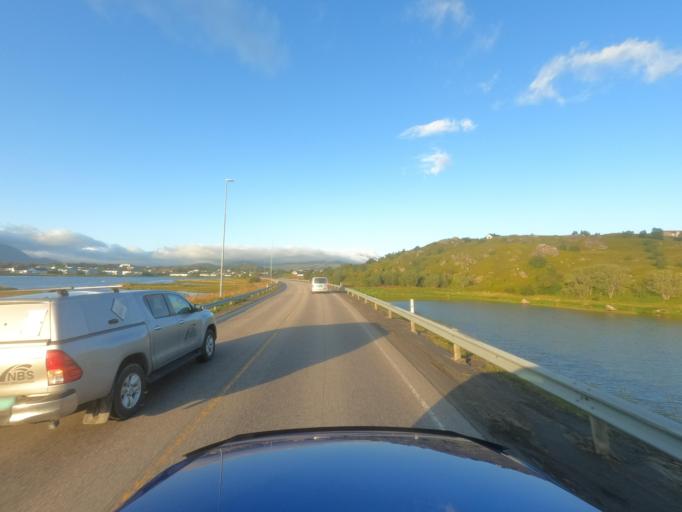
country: NO
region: Nordland
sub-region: Vestvagoy
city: Leknes
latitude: 68.1384
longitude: 13.5954
